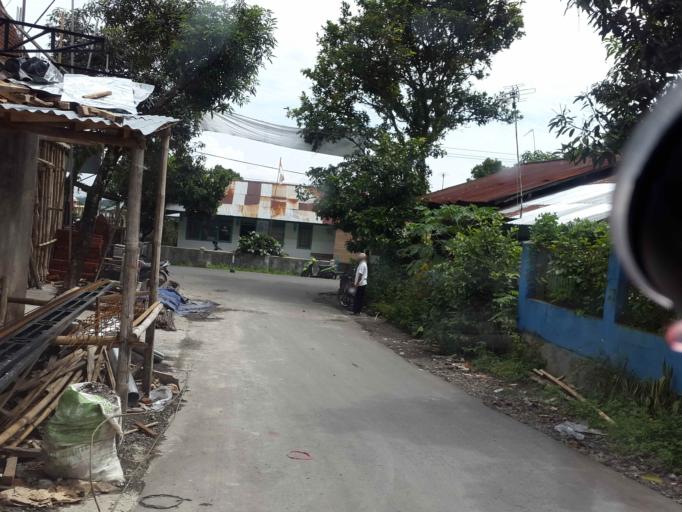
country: ID
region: Central Java
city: Randudongkal
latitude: -7.1273
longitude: 109.2268
